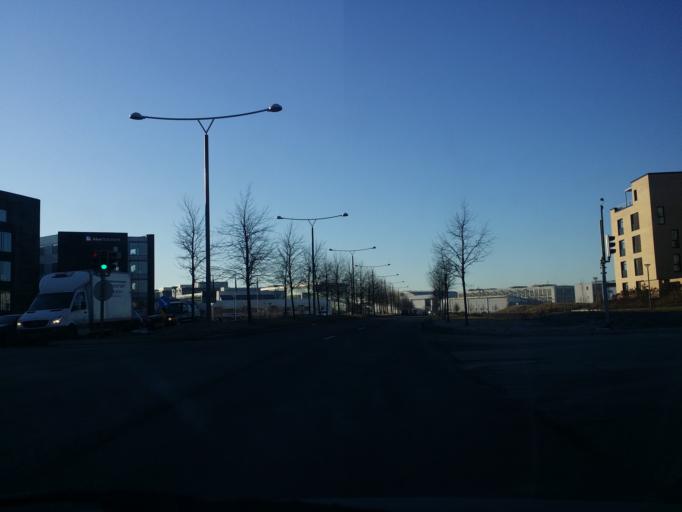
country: NO
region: Akershus
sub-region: Baerum
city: Lysaker
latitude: 59.8979
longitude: 10.6261
